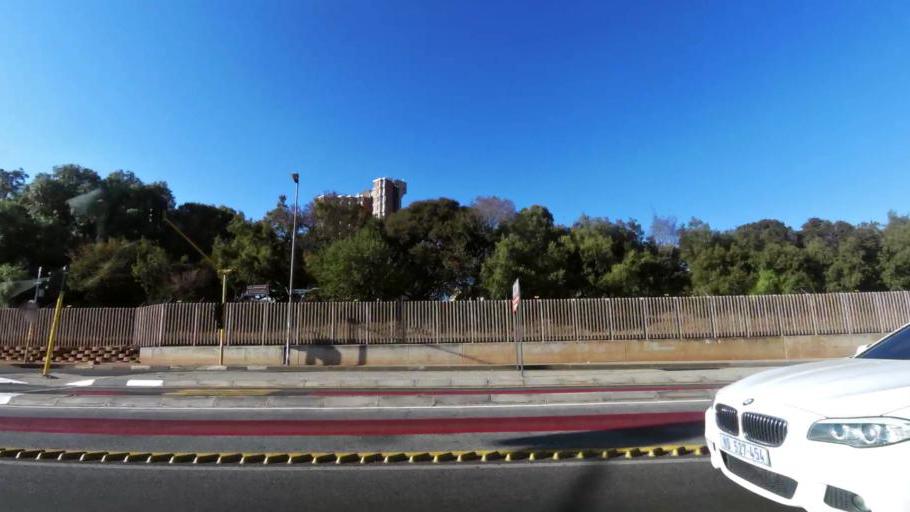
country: ZA
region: Gauteng
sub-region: City of Johannesburg Metropolitan Municipality
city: Johannesburg
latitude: -26.1819
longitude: 27.9931
